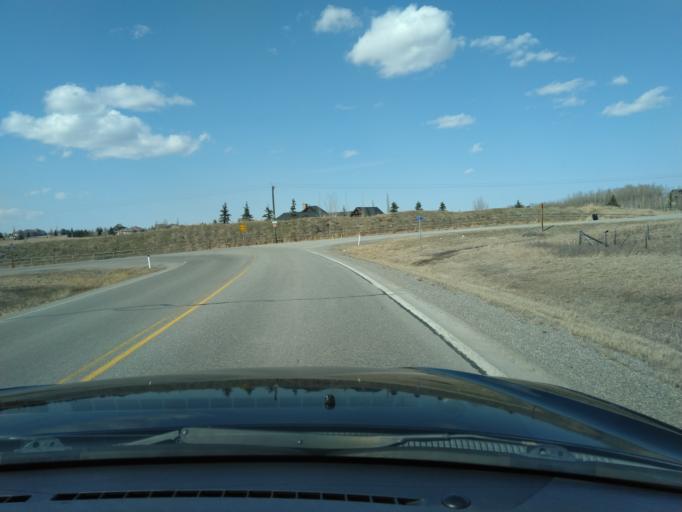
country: CA
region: Alberta
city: Cochrane
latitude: 51.0956
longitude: -114.2998
